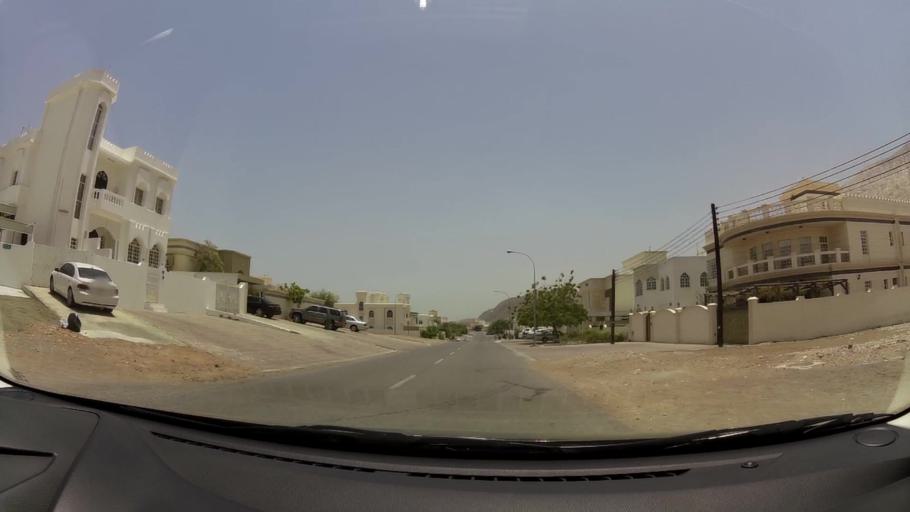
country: OM
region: Muhafazat Masqat
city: Bawshar
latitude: 23.5602
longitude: 58.4128
